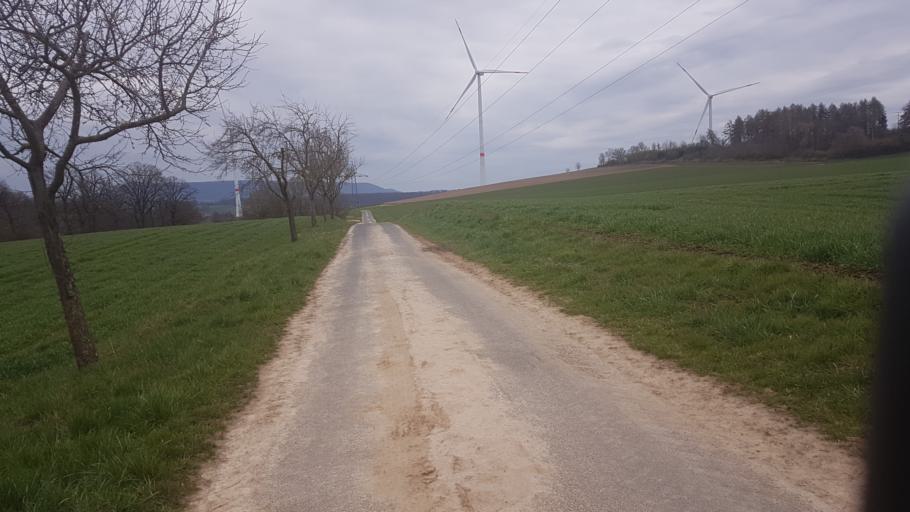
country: DE
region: Lower Saxony
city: Bad Munder am Deister
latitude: 52.1394
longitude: 9.4192
